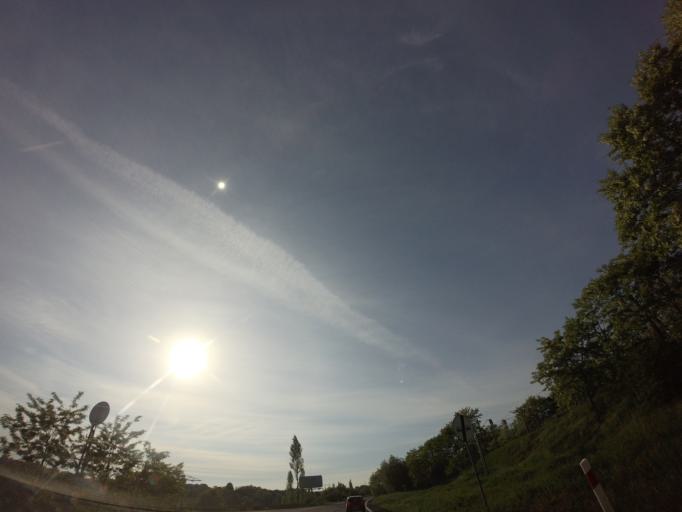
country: PL
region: West Pomeranian Voivodeship
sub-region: Szczecin
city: Szczecin
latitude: 53.3843
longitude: 14.5311
